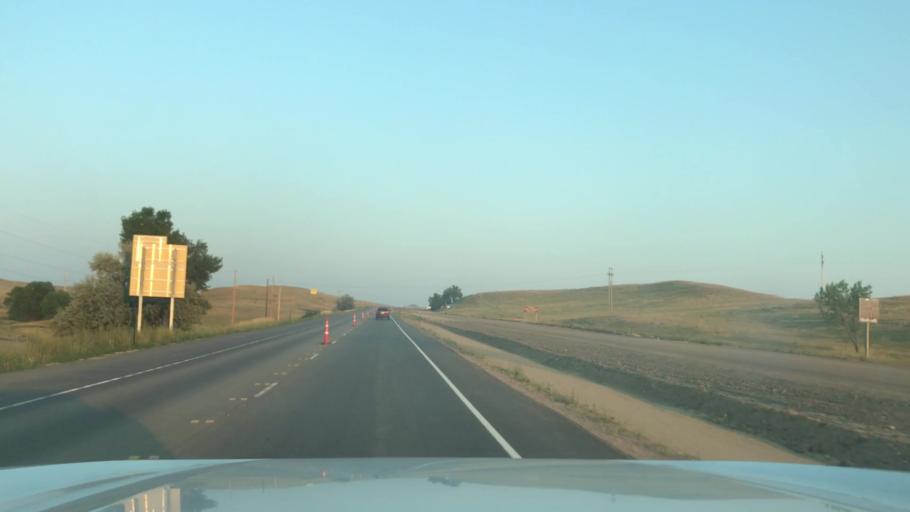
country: US
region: Wyoming
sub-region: Sheridan County
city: Sheridan
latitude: 44.8273
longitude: -106.9514
